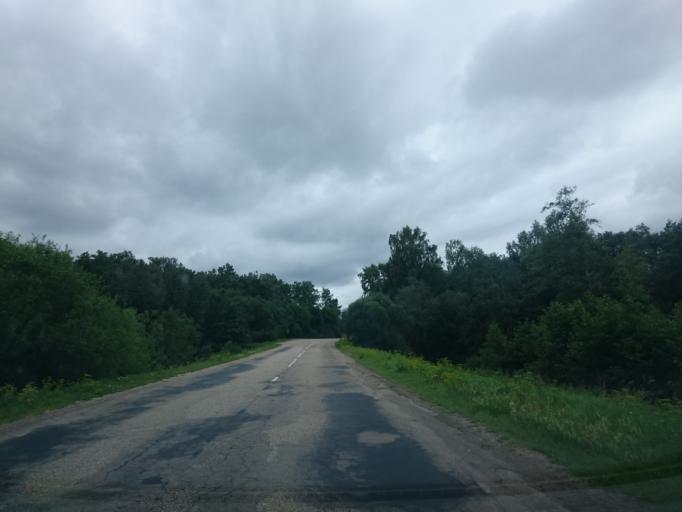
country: LV
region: Pavilostas
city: Pavilosta
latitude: 56.8643
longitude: 21.2243
